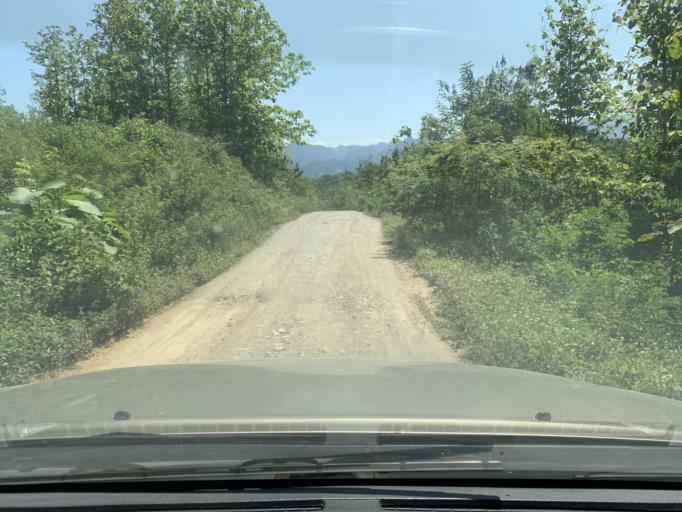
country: LA
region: Louangphabang
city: Louangphabang
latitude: 19.8981
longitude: 102.2132
